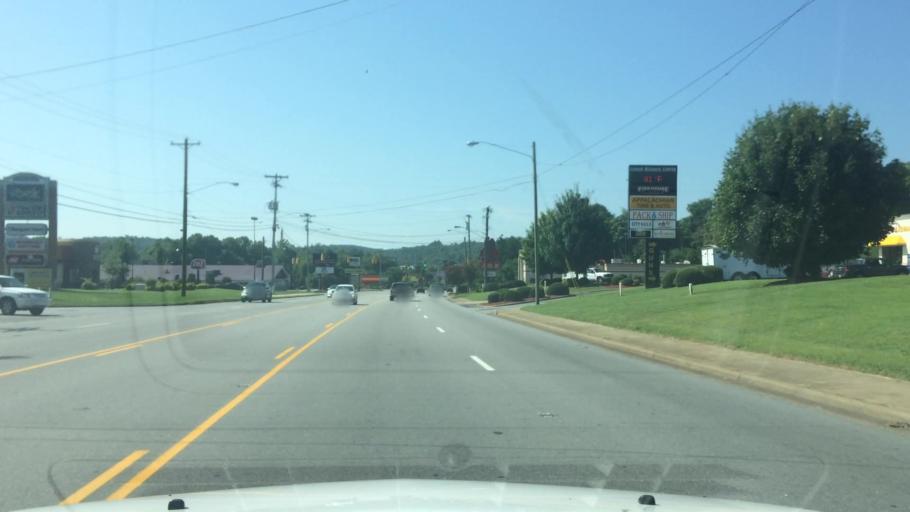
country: US
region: North Carolina
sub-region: Caldwell County
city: Lenoir
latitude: 35.9208
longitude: -81.5250
